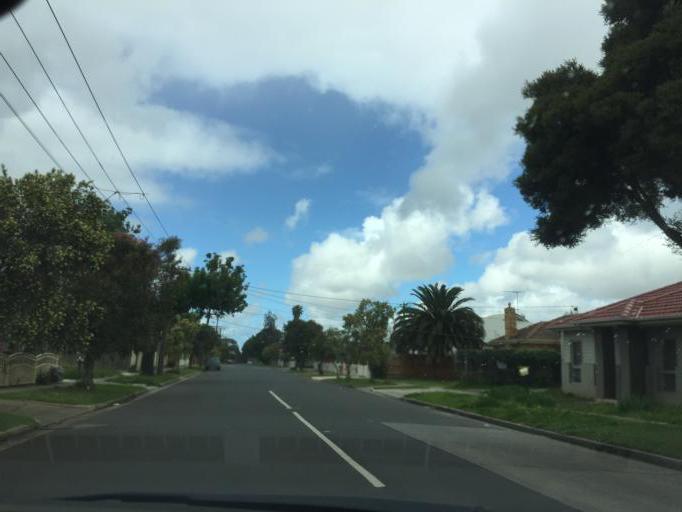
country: AU
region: Victoria
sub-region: Brimbank
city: Sunshine West
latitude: -37.7820
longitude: 144.8225
